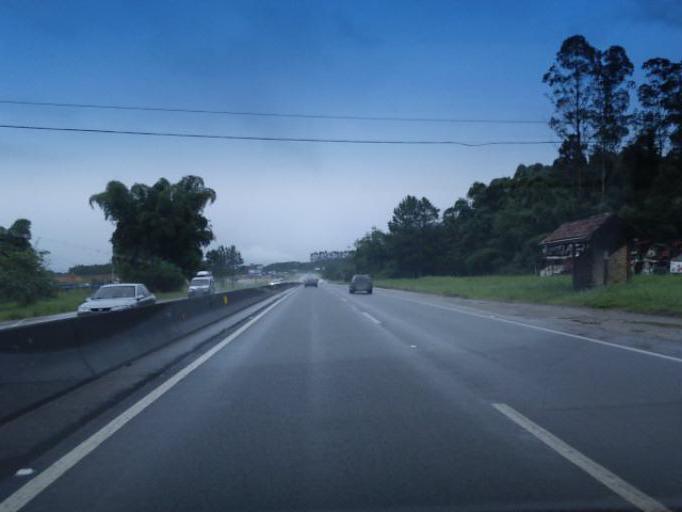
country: BR
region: Santa Catarina
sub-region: Barra Velha
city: Barra Velha
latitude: -26.4718
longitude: -48.7441
